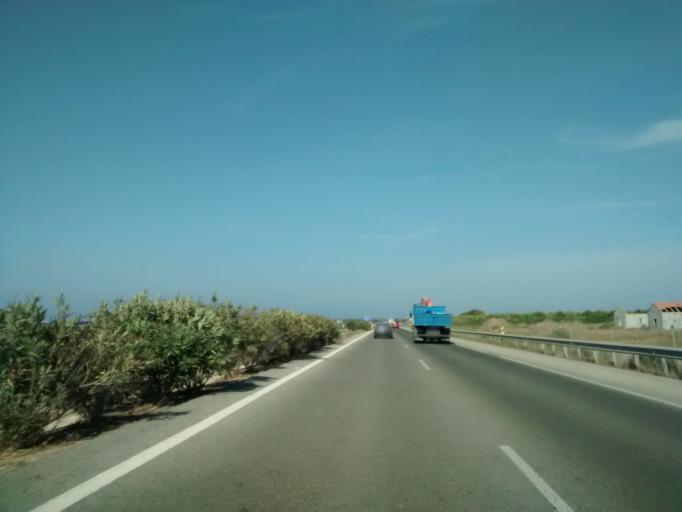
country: ES
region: Andalusia
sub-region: Provincia de Cadiz
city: Conil de la Frontera
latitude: 36.3546
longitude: -6.0796
